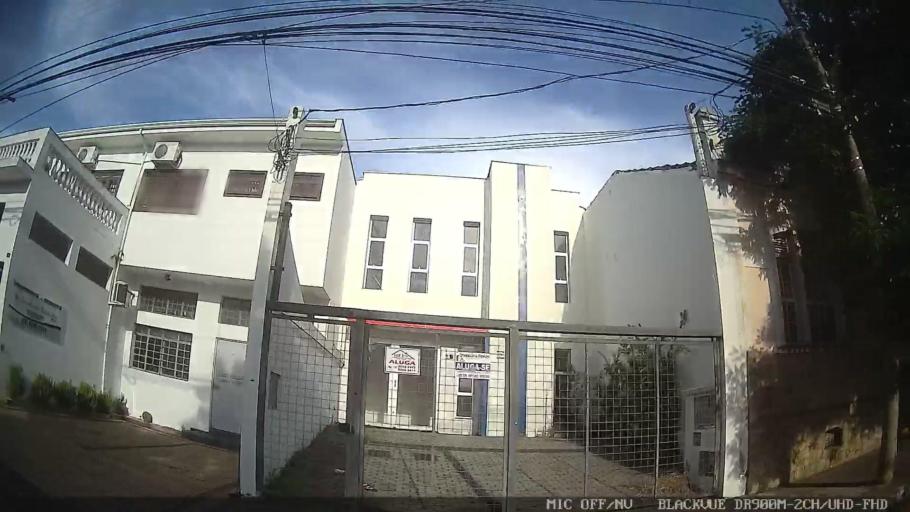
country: BR
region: Sao Paulo
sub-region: Tiete
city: Tiete
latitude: -23.1047
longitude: -47.7141
